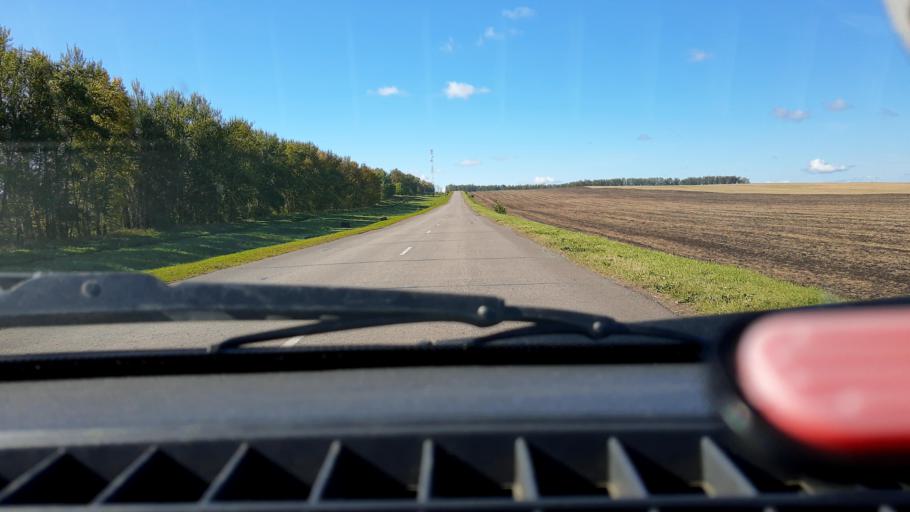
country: RU
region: Bashkortostan
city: Kushnarenkovo
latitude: 55.0817
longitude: 55.4724
